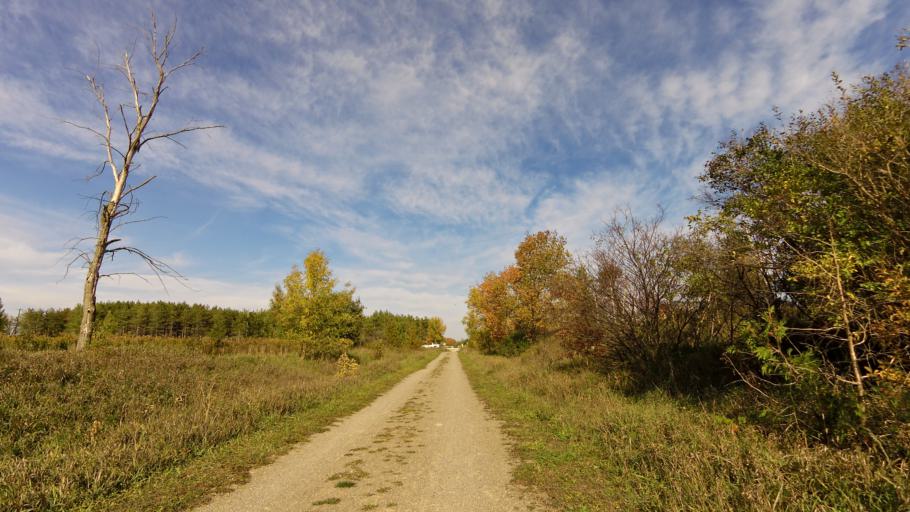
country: CA
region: Ontario
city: Orangeville
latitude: 43.7922
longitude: -80.0485
